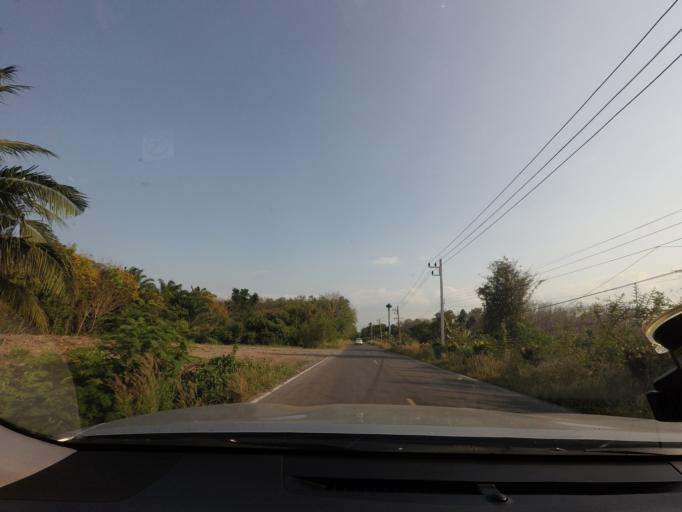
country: TH
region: Surat Thani
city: Phrasaeng
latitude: 8.5792
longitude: 99.2801
